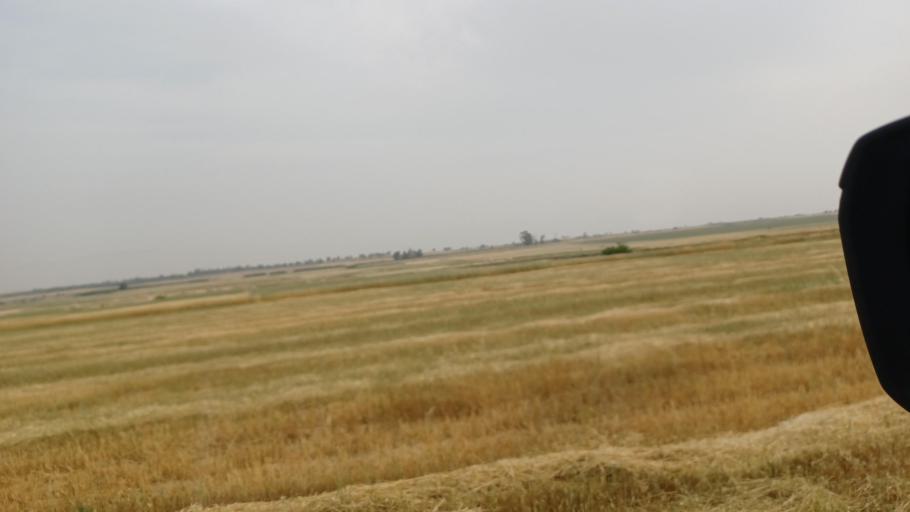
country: CY
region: Lefkosia
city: Mammari
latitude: 35.1708
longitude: 33.2295
